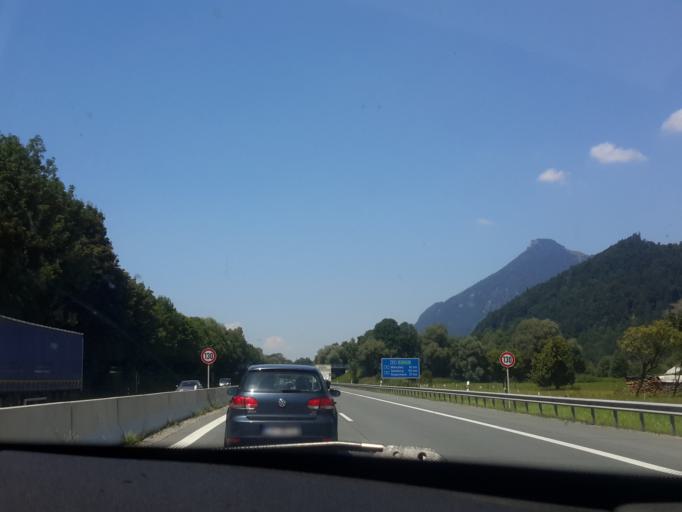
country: DE
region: Bavaria
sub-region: Upper Bavaria
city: Oberaudorf
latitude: 47.6491
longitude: 12.1883
